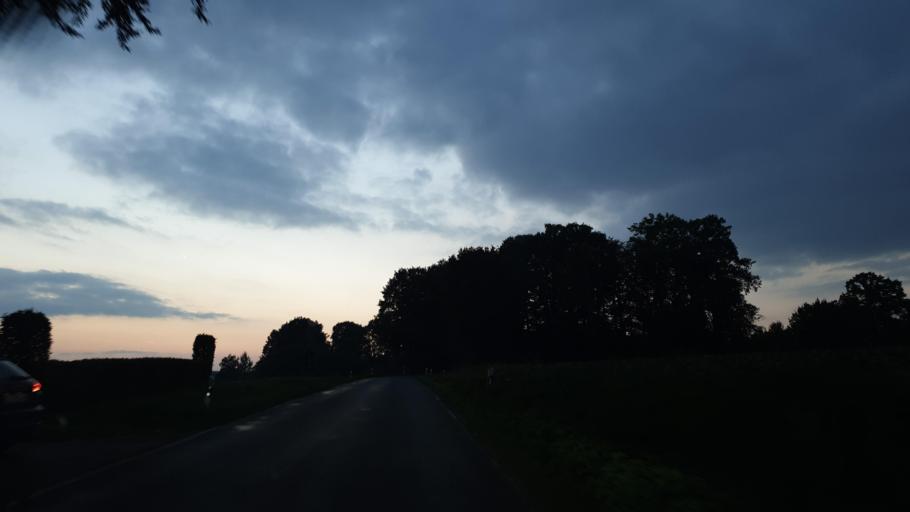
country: DE
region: North Rhine-Westphalia
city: Loehne
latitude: 52.2354
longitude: 8.6824
